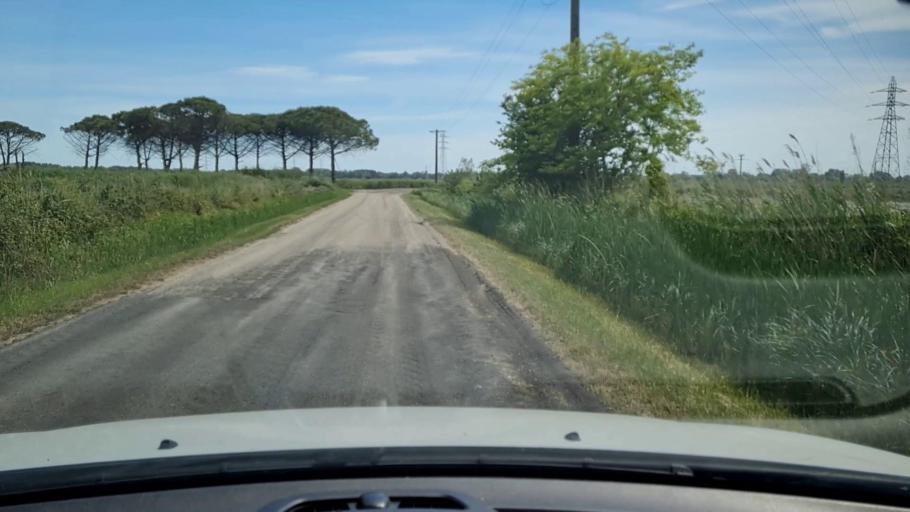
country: FR
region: Languedoc-Roussillon
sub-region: Departement du Gard
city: Saint-Gilles
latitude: 43.5744
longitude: 4.3970
